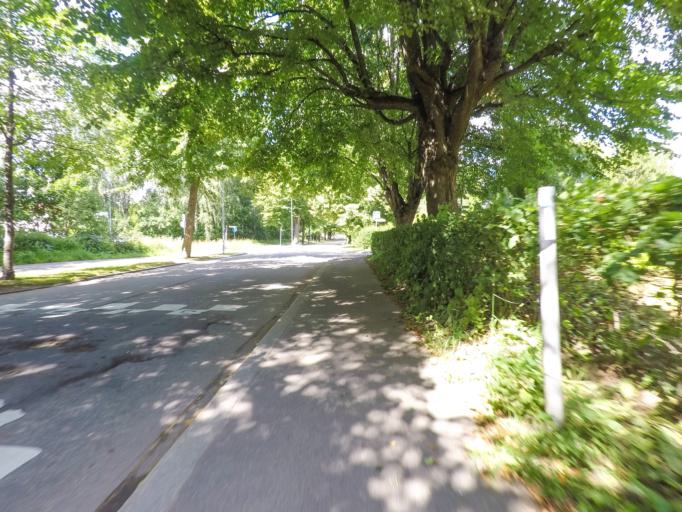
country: FI
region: Uusimaa
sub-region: Helsinki
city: Vantaa
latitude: 60.2169
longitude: 25.0961
